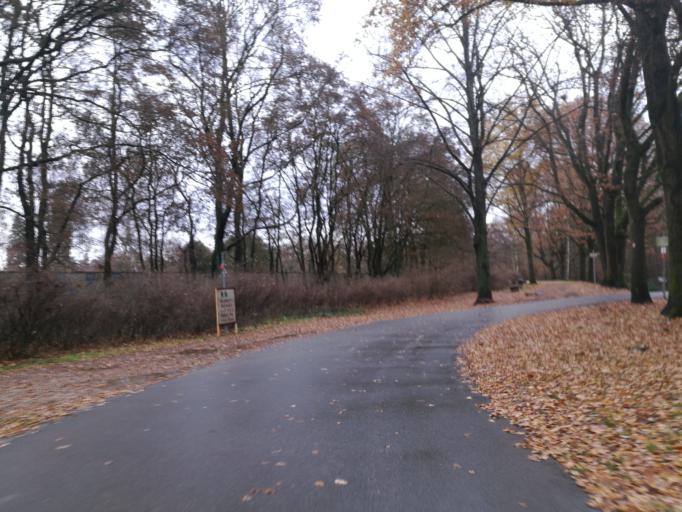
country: DE
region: Bavaria
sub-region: Regierungsbezirk Mittelfranken
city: Wetzendorf
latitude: 49.4650
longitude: 11.0341
